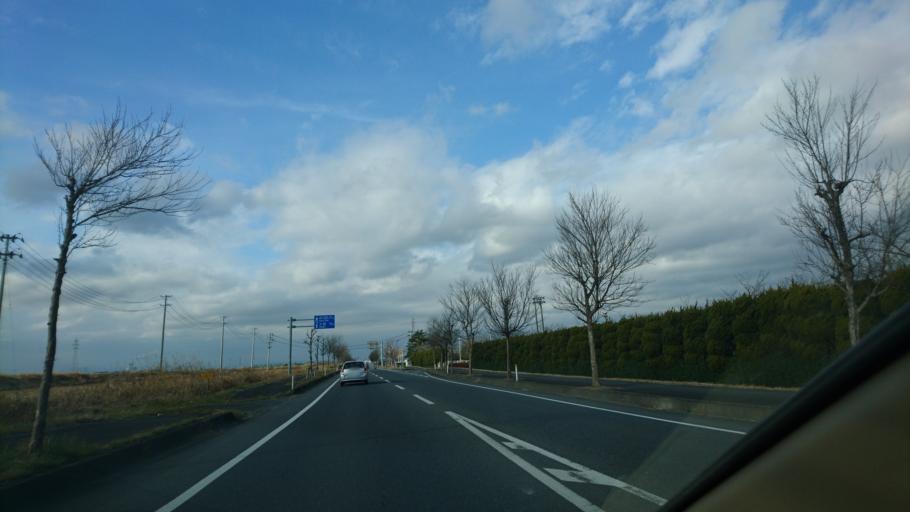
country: JP
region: Miyagi
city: Wakuya
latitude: 38.5348
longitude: 141.1209
